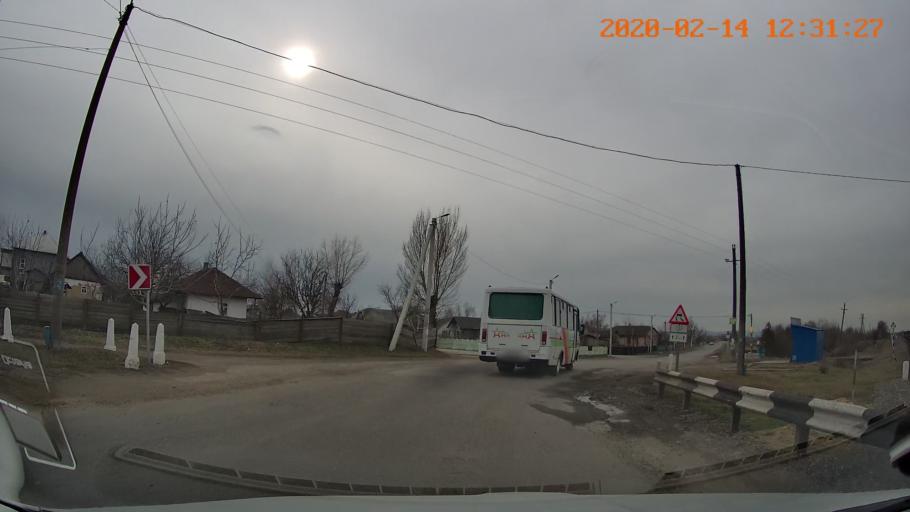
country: RO
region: Botosani
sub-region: Comuna Darabani
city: Bajura
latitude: 48.2484
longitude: 26.5569
